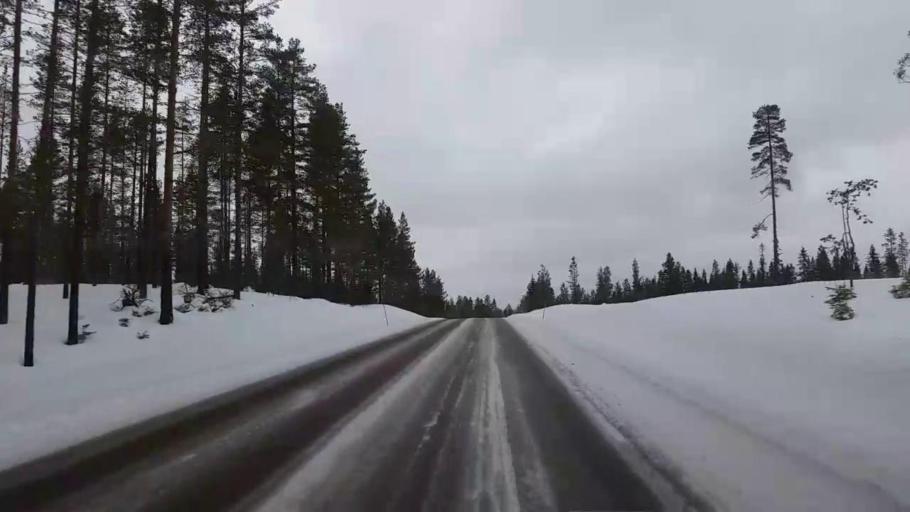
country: SE
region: Jaemtland
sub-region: Bergs Kommun
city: Hoverberg
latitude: 62.4254
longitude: 14.6016
